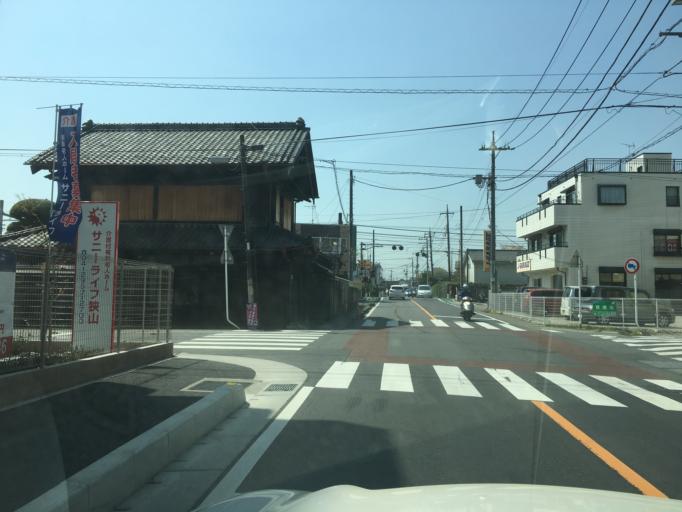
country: JP
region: Saitama
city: Sayama
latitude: 35.8343
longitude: 139.4263
